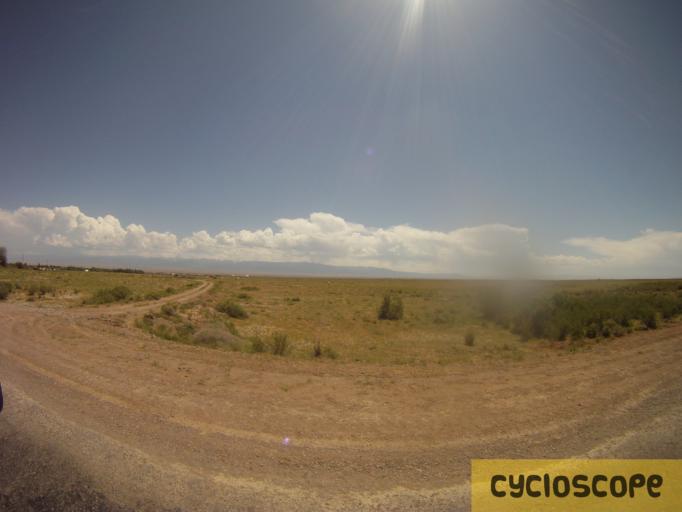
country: KZ
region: Almaty Oblysy
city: Kegen
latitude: 43.5370
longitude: 79.4449
